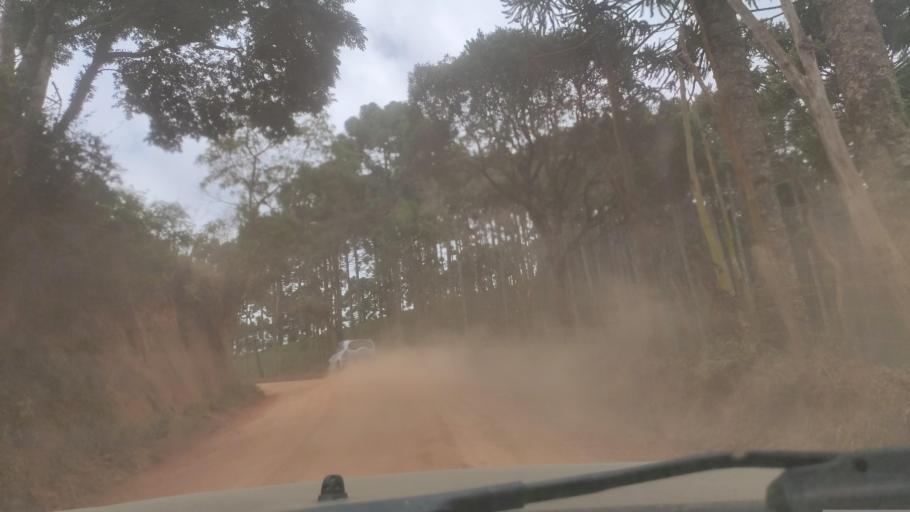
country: BR
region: Minas Gerais
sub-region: Paraisopolis
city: Paraisopolis
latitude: -22.6609
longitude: -45.8969
